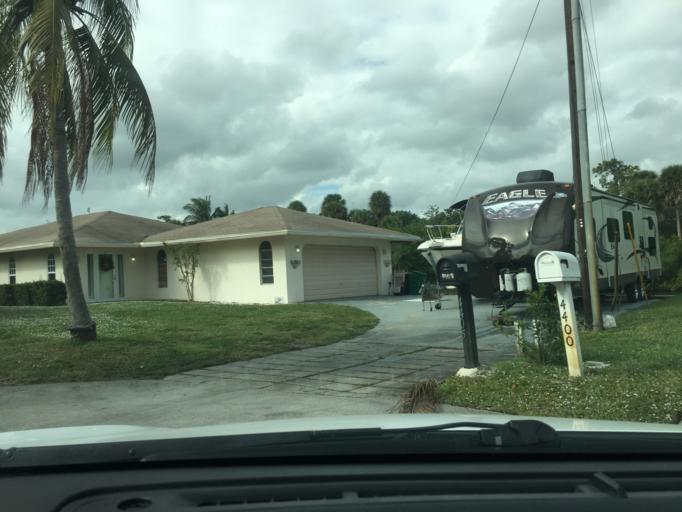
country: US
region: Florida
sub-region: Broward County
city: Dania Beach
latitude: 26.0676
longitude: -80.1756
